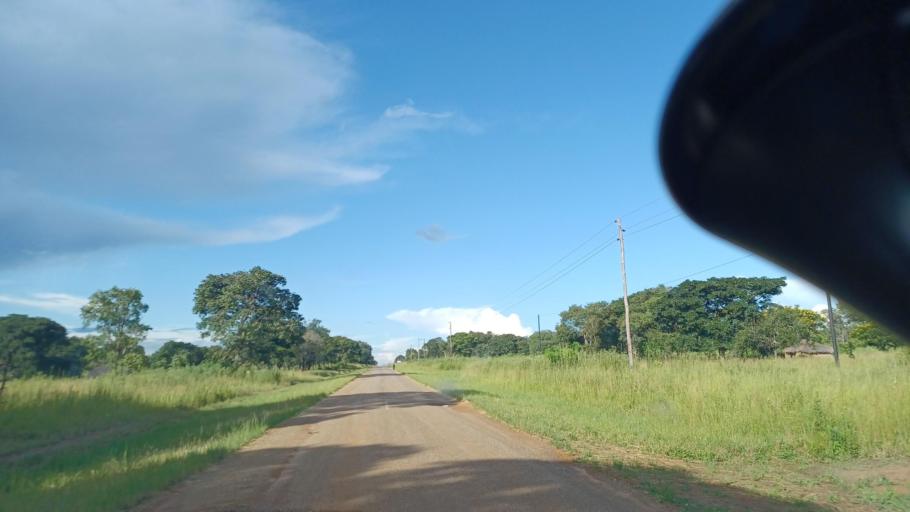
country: ZM
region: North-Western
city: Kabompo
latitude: -13.3040
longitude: 24.4536
